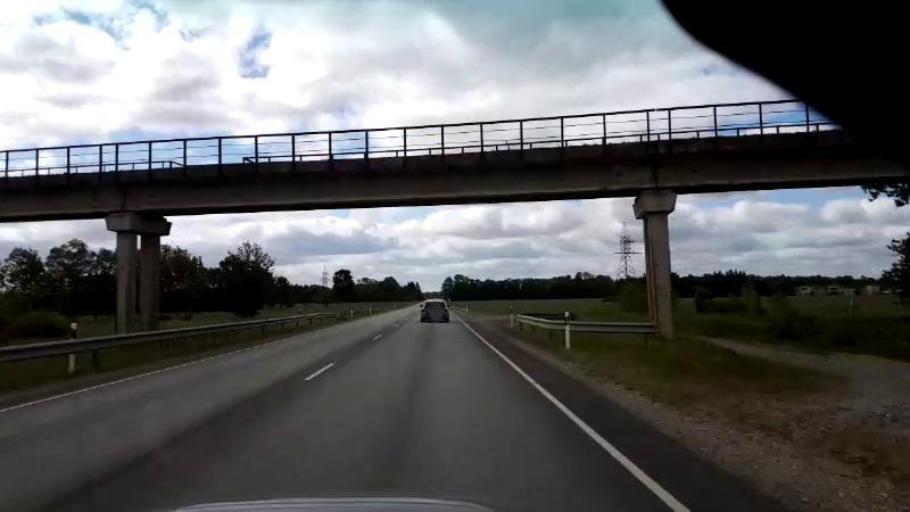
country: EE
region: Paernumaa
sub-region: Halinga vald
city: Parnu-Jaagupi
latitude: 58.5804
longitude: 24.5123
